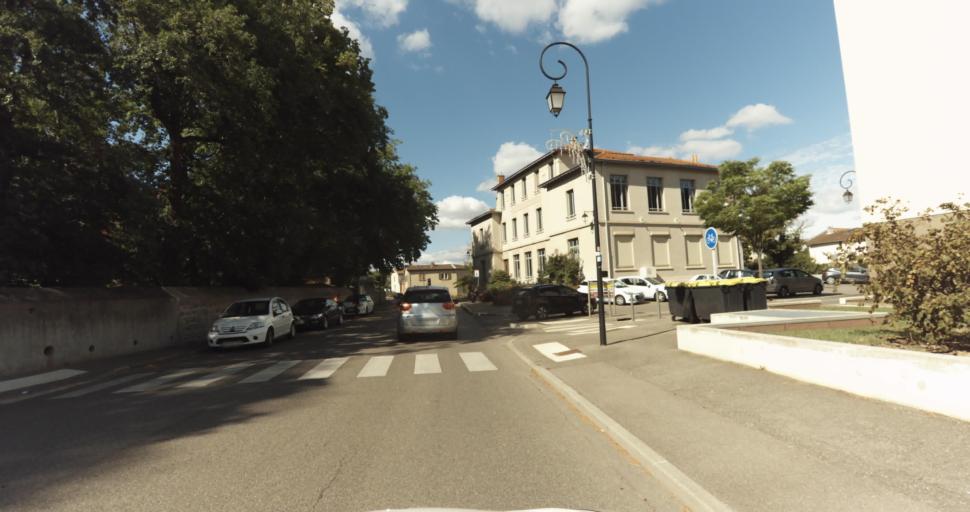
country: FR
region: Rhone-Alpes
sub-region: Departement du Rhone
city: Chaponost
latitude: 45.7095
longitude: 4.7424
